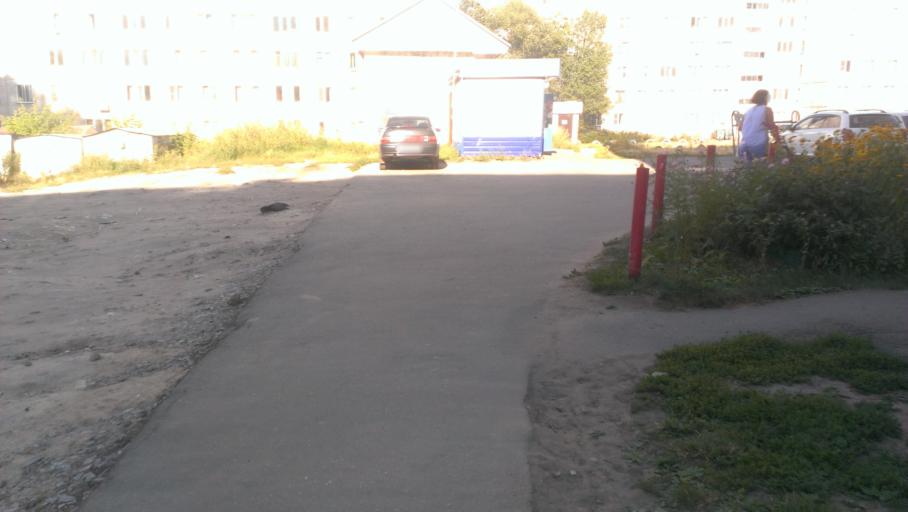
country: RU
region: Altai Krai
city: Novosilikatnyy
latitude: 53.3059
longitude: 83.6230
